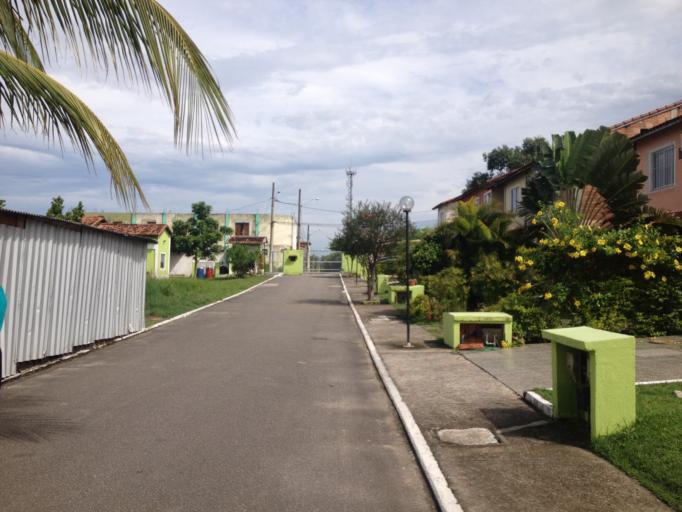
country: BR
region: Rio de Janeiro
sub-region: Queimados
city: Queimados
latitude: -22.7133
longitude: -43.5606
